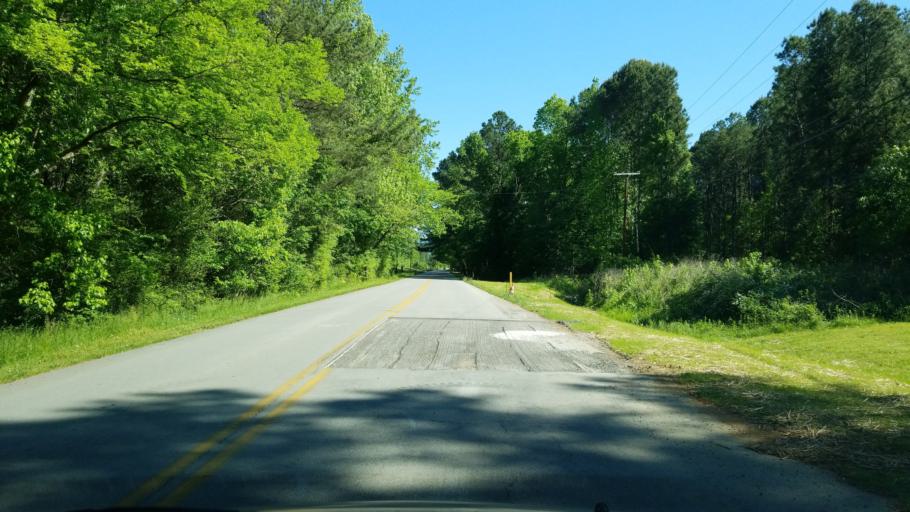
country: US
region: Tennessee
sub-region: Hamilton County
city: Chattanooga
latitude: 35.0350
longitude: -85.3348
